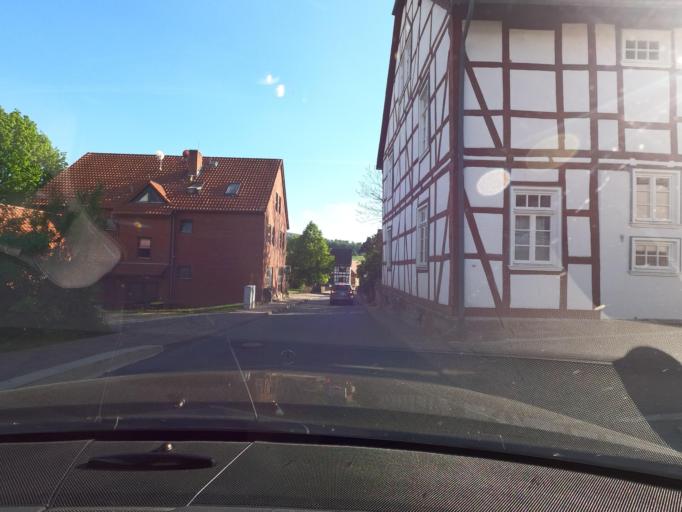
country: DE
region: Hesse
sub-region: Regierungsbezirk Kassel
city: Wolfhagen
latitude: 51.3409
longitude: 9.2313
